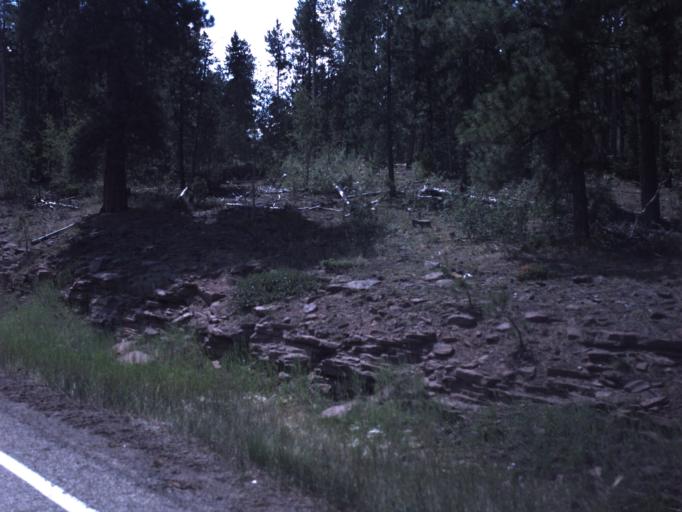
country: US
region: Utah
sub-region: Daggett County
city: Manila
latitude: 40.8527
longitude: -109.6756
